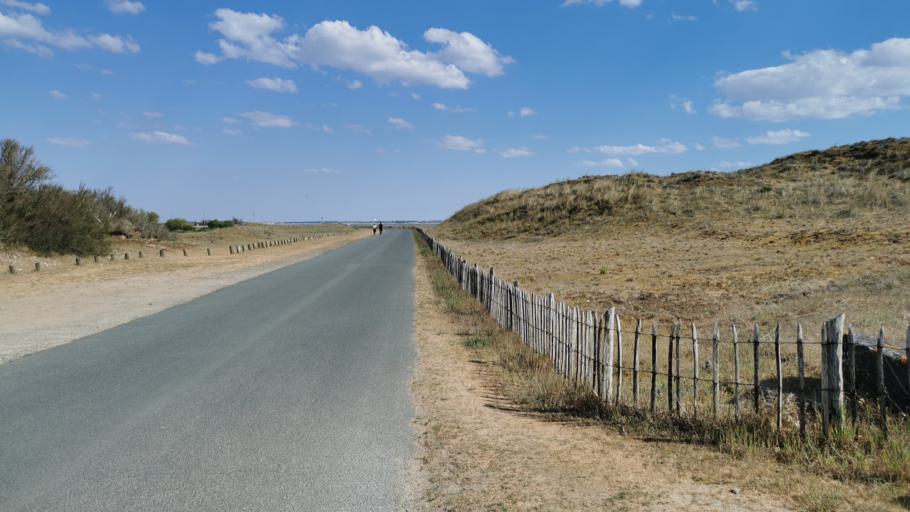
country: FR
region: Poitou-Charentes
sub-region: Departement de la Charente-Maritime
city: Nieul-sur-Mer
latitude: 46.2708
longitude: -1.2110
